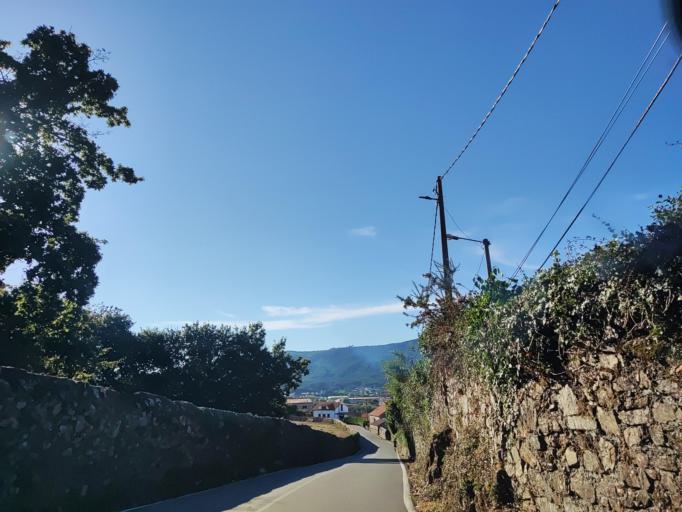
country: ES
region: Galicia
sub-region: Provincia da Coruna
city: Boiro
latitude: 42.5941
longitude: -8.9304
